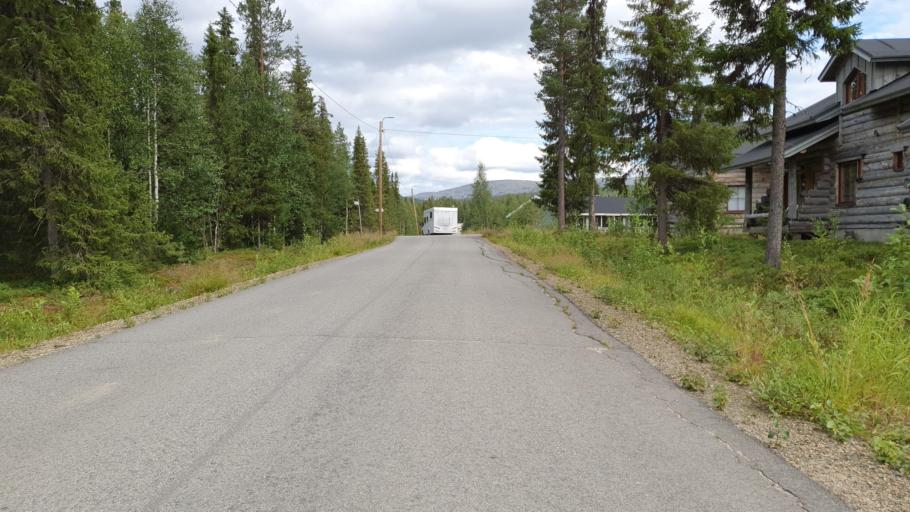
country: FI
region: Lapland
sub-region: Tunturi-Lappi
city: Kolari
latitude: 67.6018
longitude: 24.1468
